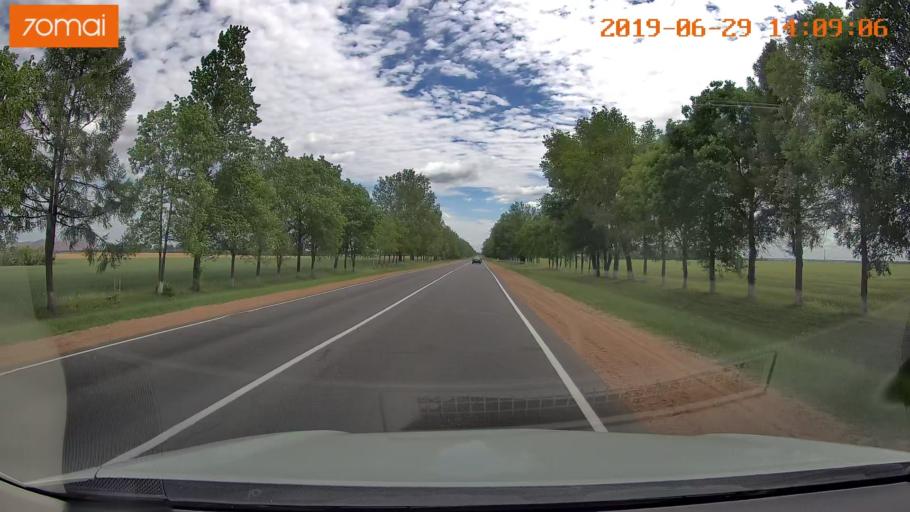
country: BY
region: Minsk
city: Salihorsk
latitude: 52.8438
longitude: 27.4818
